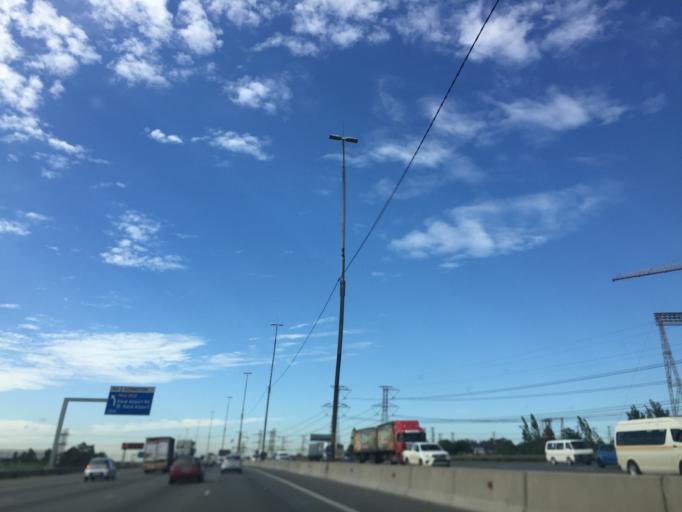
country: ZA
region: Gauteng
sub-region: Ekurhuleni Metropolitan Municipality
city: Germiston
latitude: -26.2242
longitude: 28.1269
